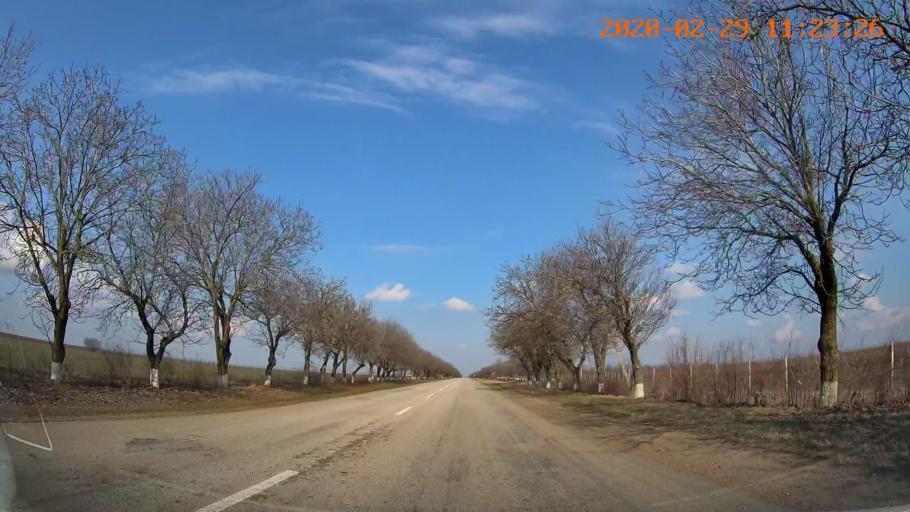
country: MD
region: Telenesti
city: Cocieri
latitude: 47.4081
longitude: 29.1589
